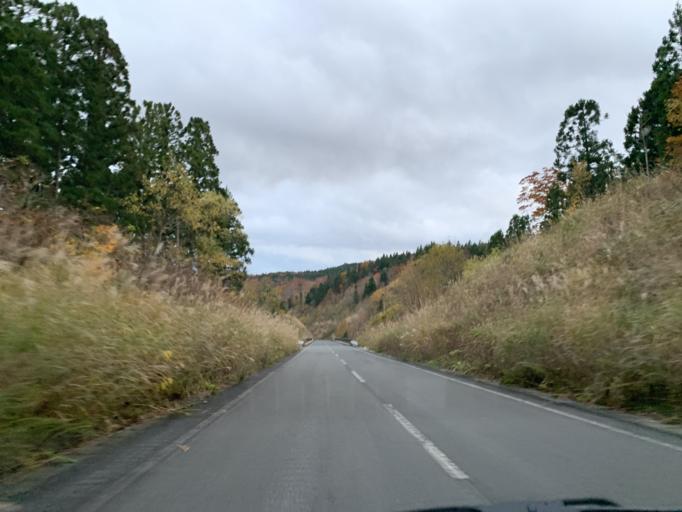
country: JP
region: Iwate
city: Mizusawa
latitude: 39.0357
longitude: 140.8570
